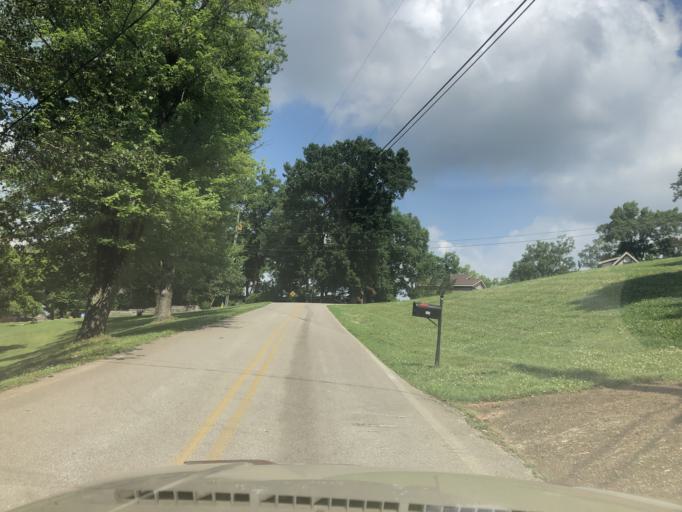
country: US
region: Tennessee
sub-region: Wilson County
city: Green Hill
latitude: 36.2443
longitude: -86.5888
